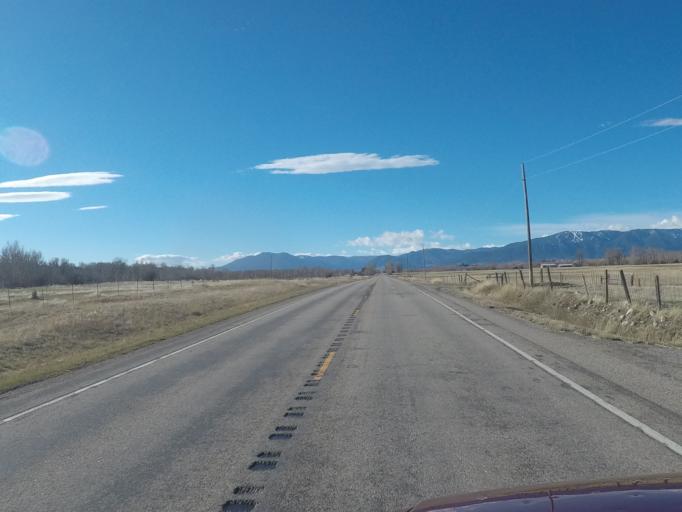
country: US
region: Montana
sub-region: Carbon County
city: Red Lodge
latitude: 45.3114
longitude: -109.1969
